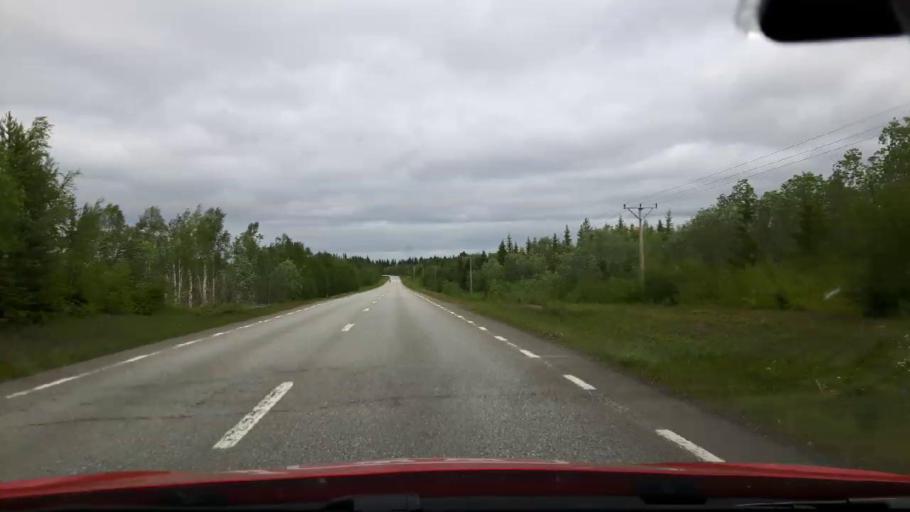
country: SE
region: Jaemtland
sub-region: Krokoms Kommun
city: Krokom
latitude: 63.5662
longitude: 14.6160
